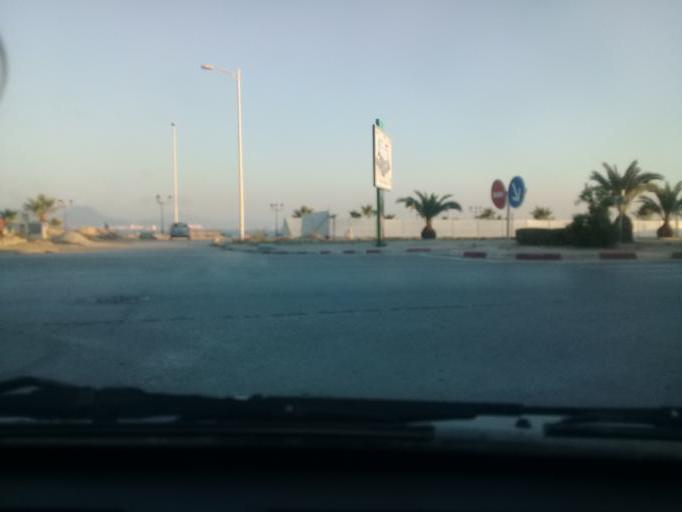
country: TN
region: Tunis
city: La Goulette
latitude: 36.8421
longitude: 10.2708
